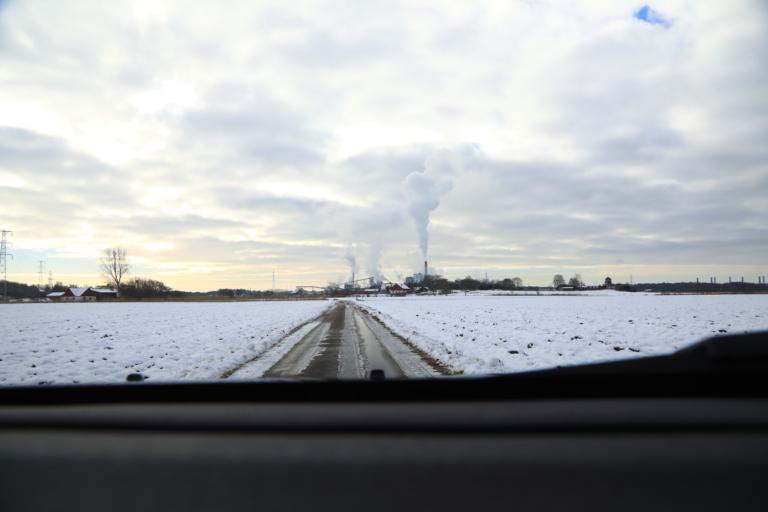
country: SE
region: Halland
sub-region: Kungsbacka Kommun
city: Frillesas
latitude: 57.2345
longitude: 12.1991
